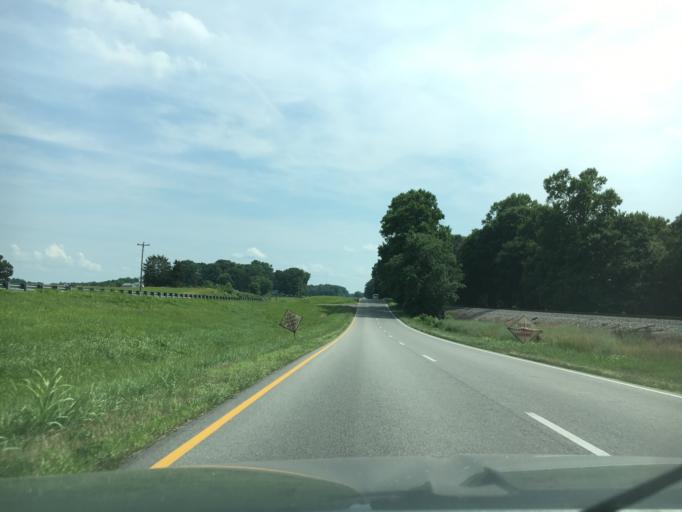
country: US
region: Virginia
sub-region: Nottoway County
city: Crewe
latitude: 37.2572
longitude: -78.1391
